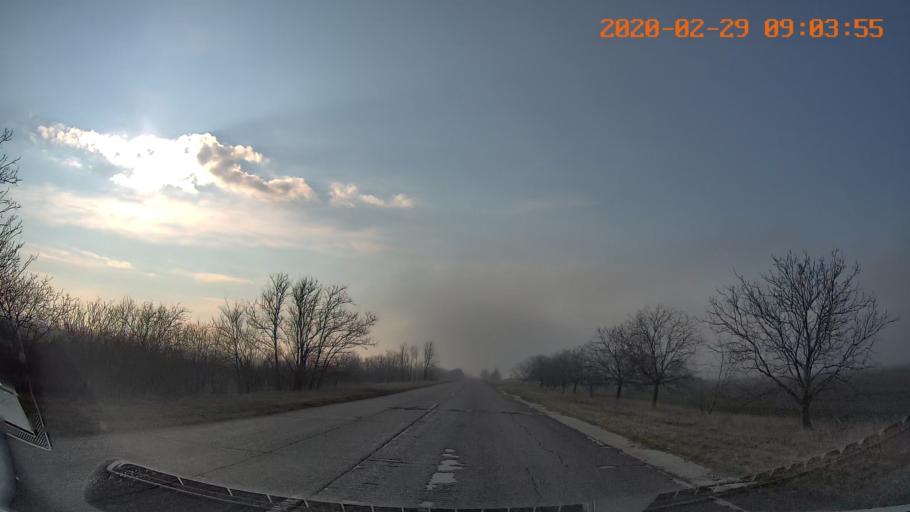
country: UA
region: Odessa
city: Velykoploske
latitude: 46.9099
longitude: 29.7337
